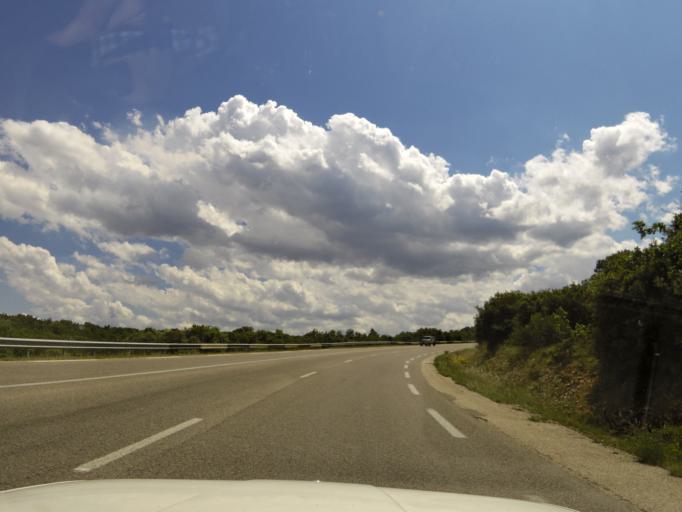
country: FR
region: Languedoc-Roussillon
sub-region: Departement du Gard
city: Sabran
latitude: 44.1324
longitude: 4.4754
